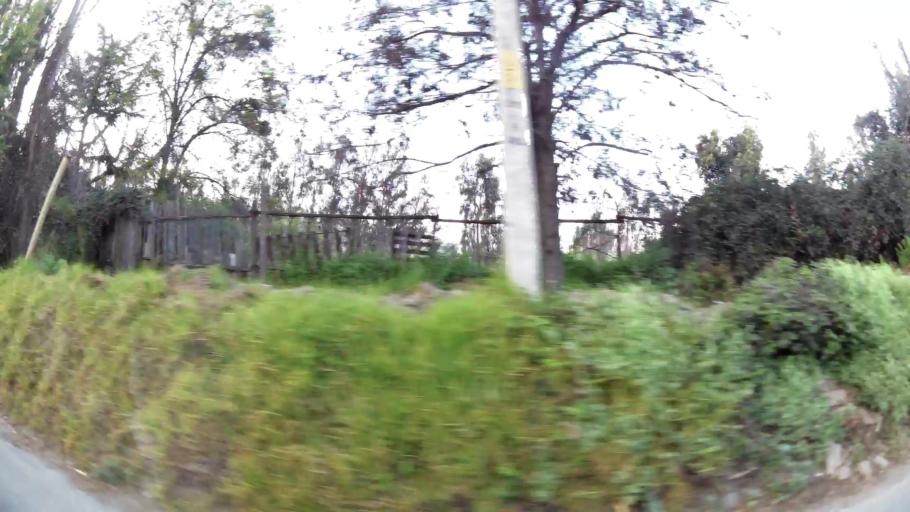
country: CL
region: Santiago Metropolitan
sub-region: Provincia de Santiago
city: Santiago
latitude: -33.3842
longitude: -70.6131
